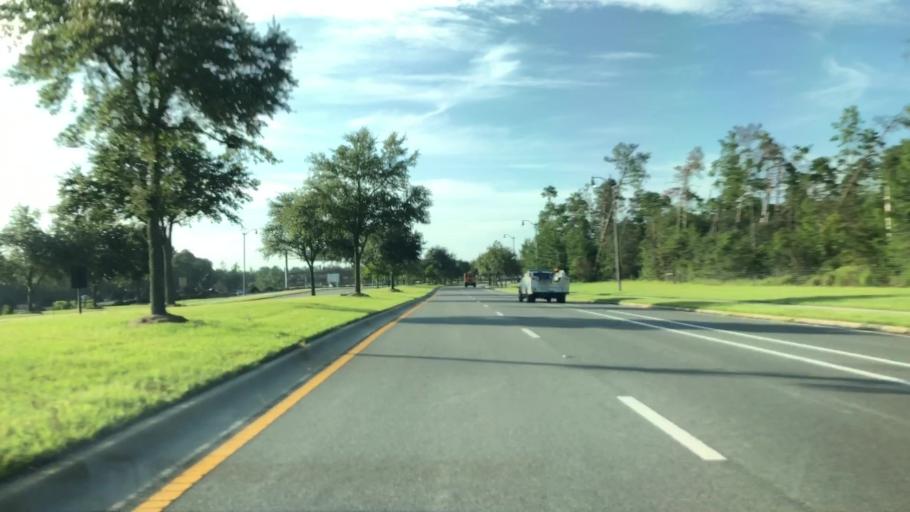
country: US
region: Florida
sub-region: Saint Johns County
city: Palm Valley
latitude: 30.1086
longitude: -81.4450
